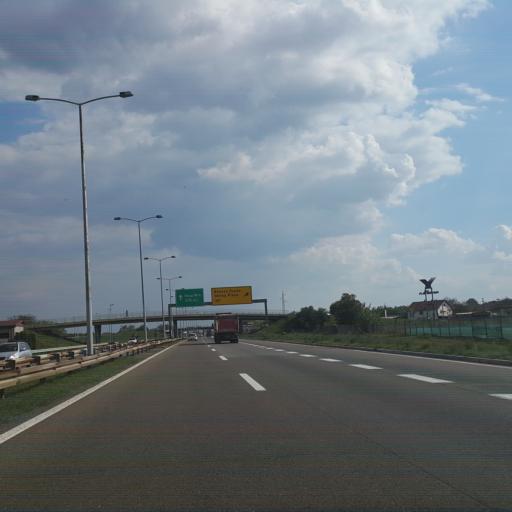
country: RS
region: Central Serbia
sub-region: Podunavski Okrug
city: Velika Plana
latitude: 44.3440
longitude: 21.0799
